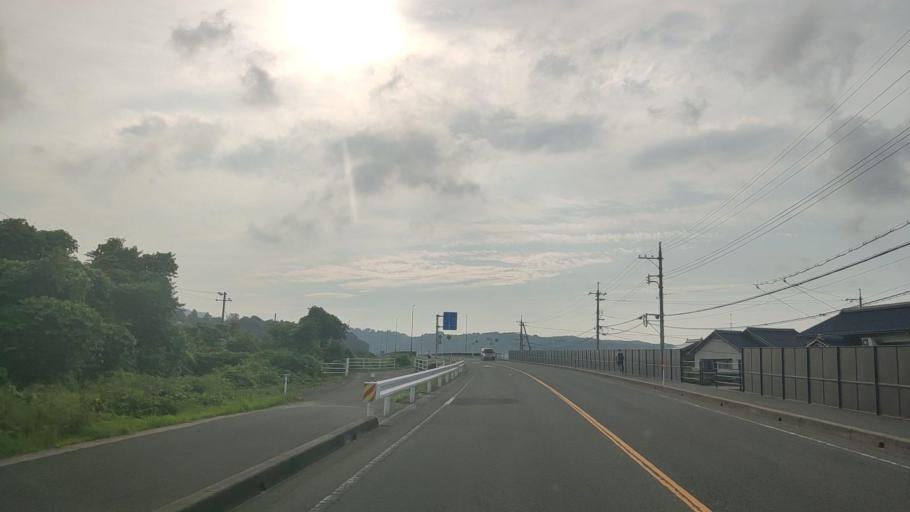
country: JP
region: Tottori
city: Kurayoshi
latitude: 35.4571
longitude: 133.8439
